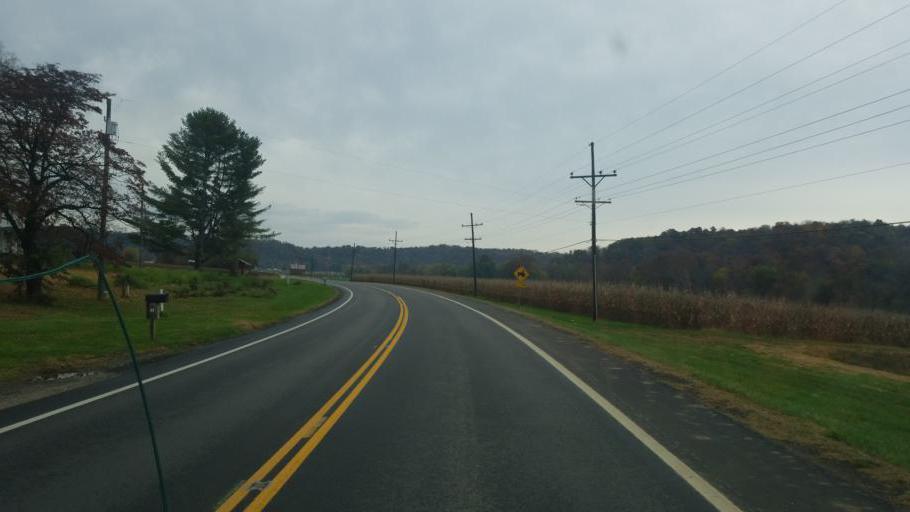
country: US
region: Ohio
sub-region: Washington County
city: Beverly
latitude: 39.5511
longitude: -81.5876
